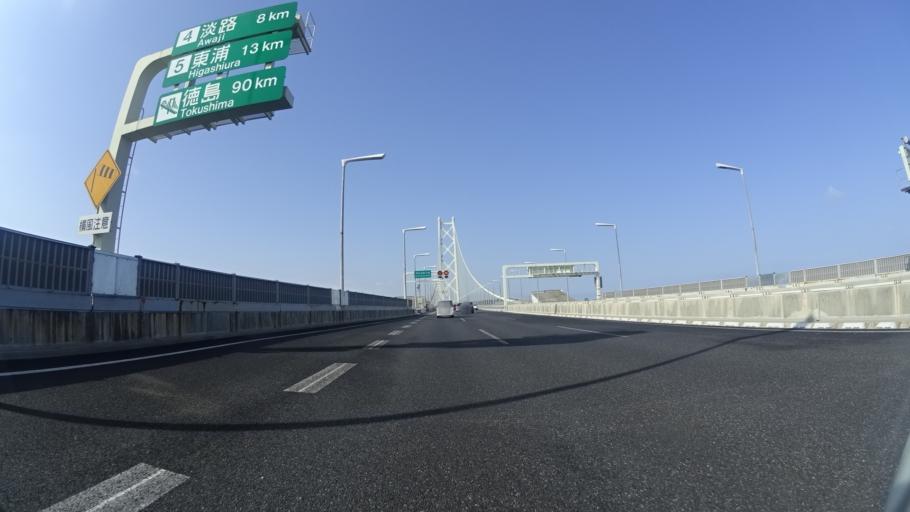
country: JP
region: Hyogo
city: Akashi
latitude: 34.6320
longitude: 135.0341
